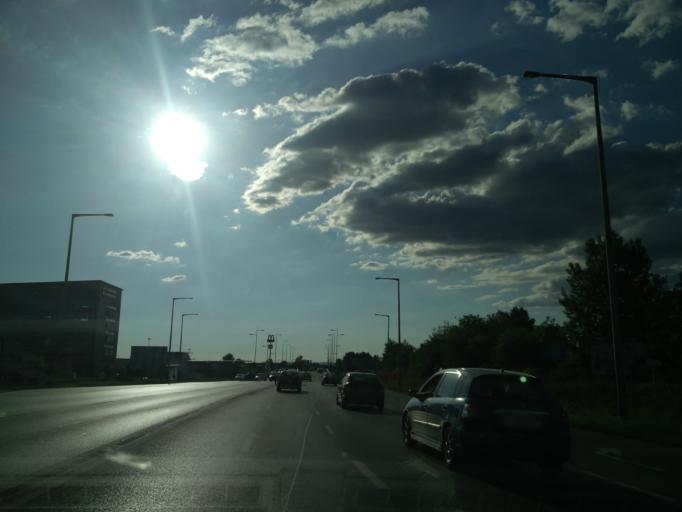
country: HU
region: Pest
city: Gyal
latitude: 47.4336
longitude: 19.2286
